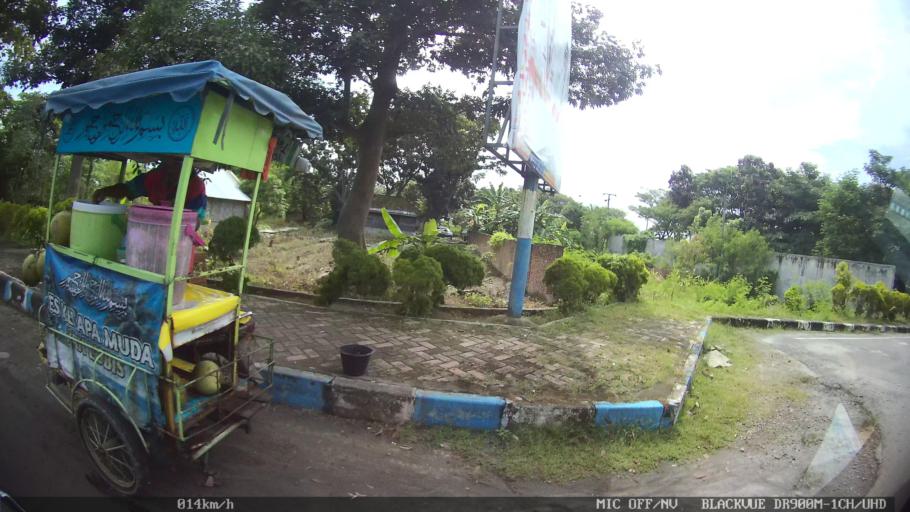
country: ID
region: North Sumatra
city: Percut
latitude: 3.5965
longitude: 98.8077
